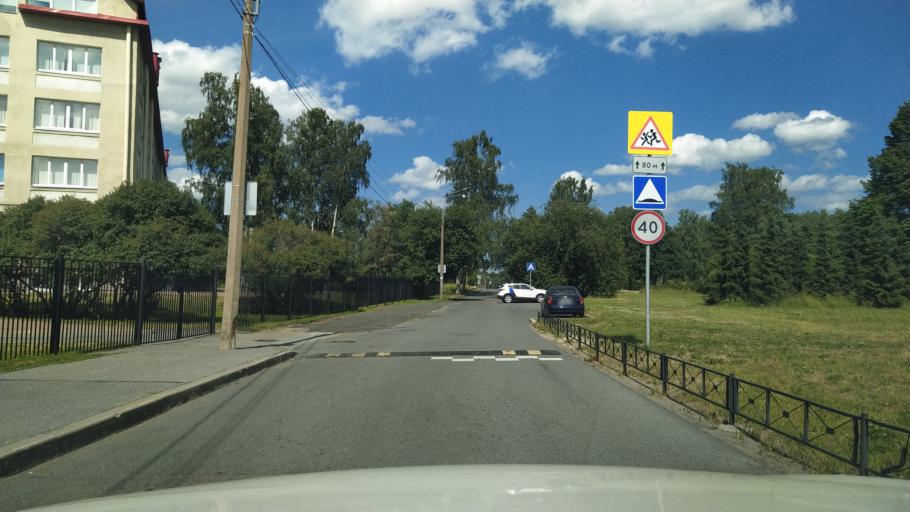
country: RU
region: Leningrad
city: Kalininskiy
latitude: 59.9952
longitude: 30.4130
